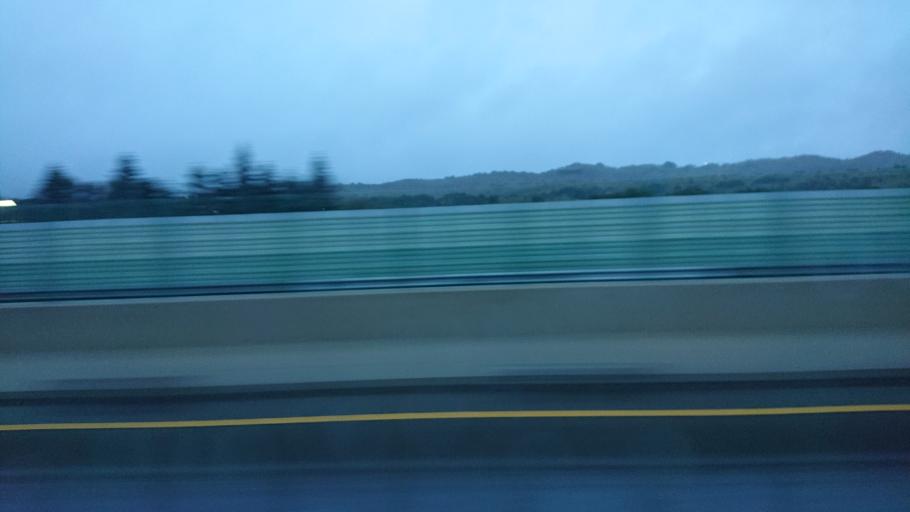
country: TW
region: Taiwan
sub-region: Miaoli
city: Miaoli
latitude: 24.5503
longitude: 120.7057
